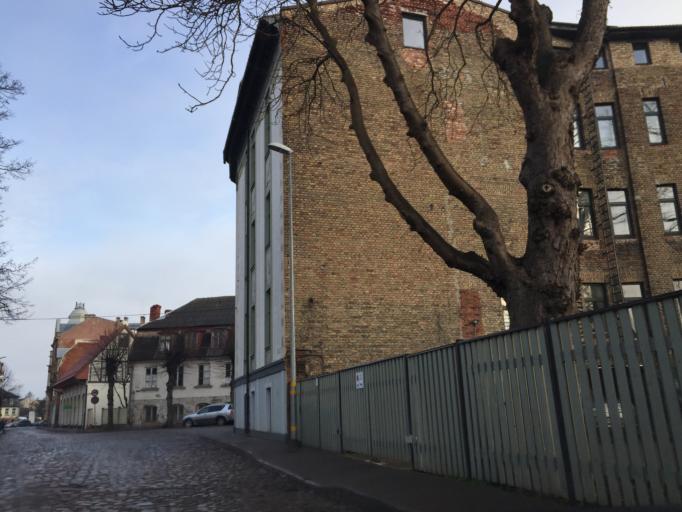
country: LV
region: Liepaja
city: Liepaja
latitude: 56.5080
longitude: 21.0072
